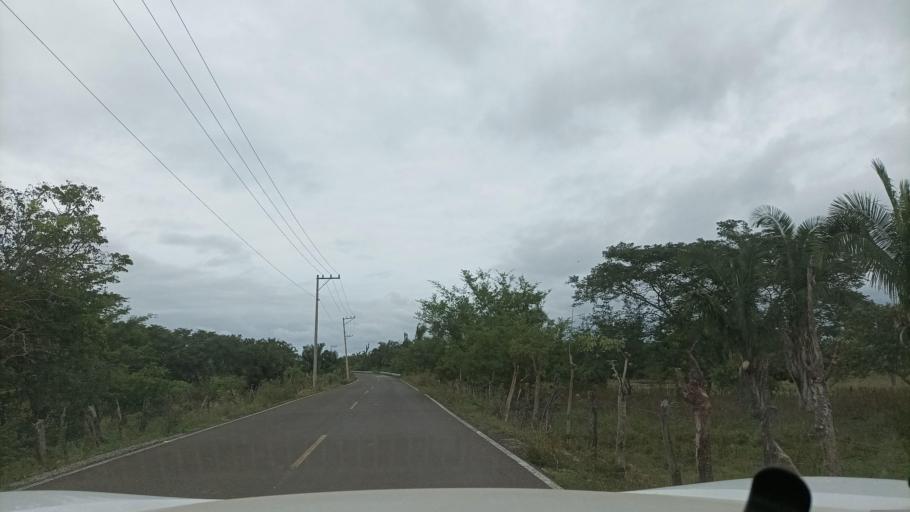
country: MX
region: Veracruz
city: Hidalgotitlan
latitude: 17.8099
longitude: -94.5613
